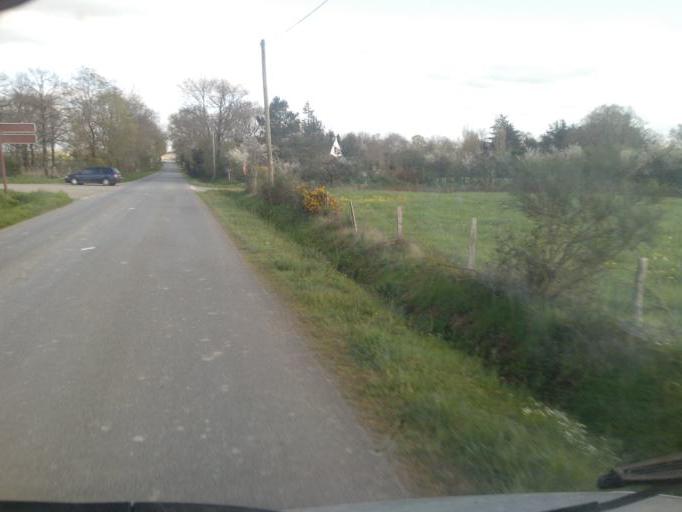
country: FR
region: Brittany
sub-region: Departement d'Ille-et-Vilaine
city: Grand-Fougeray
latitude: 47.7104
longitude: -1.7128
